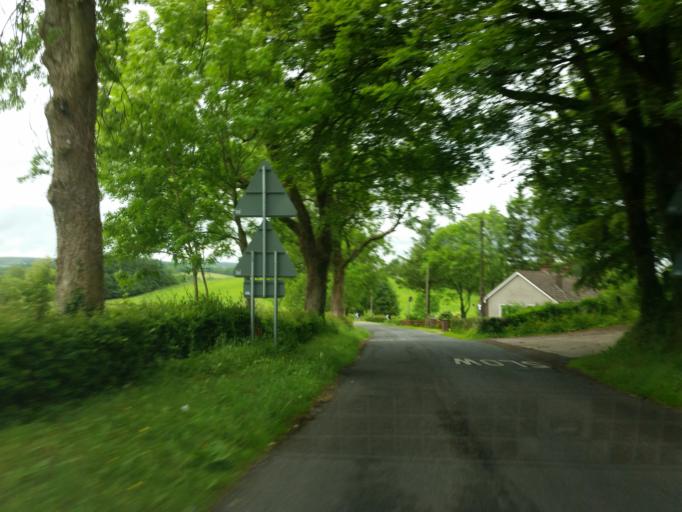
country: IE
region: Ulster
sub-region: County Monaghan
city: Clones
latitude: 54.2279
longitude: -7.2590
